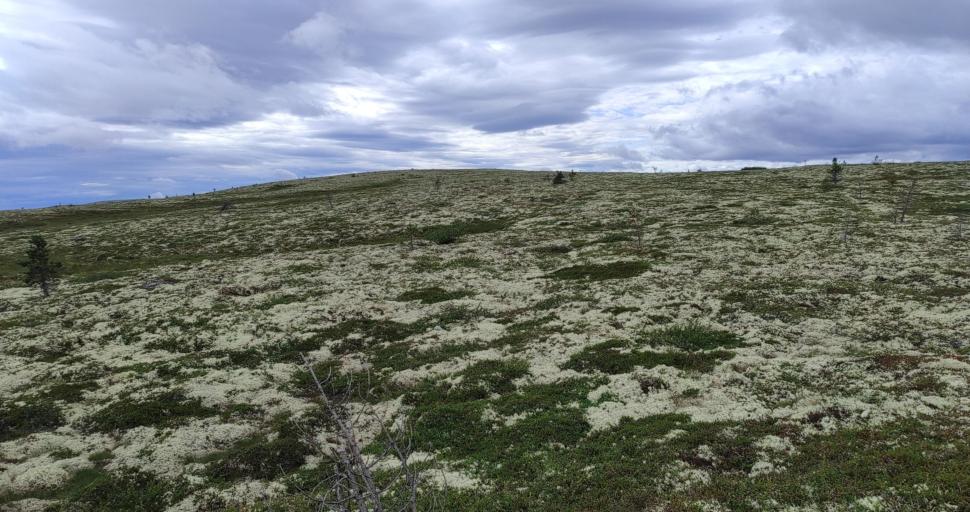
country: RU
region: Murmansk
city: Afrikanda
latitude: 67.0419
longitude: 32.9318
